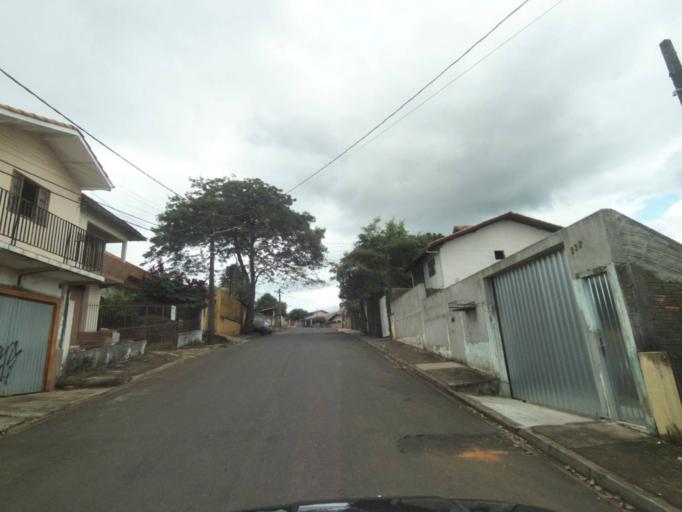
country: BR
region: Parana
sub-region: Telemaco Borba
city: Telemaco Borba
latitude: -24.3237
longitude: -50.6363
